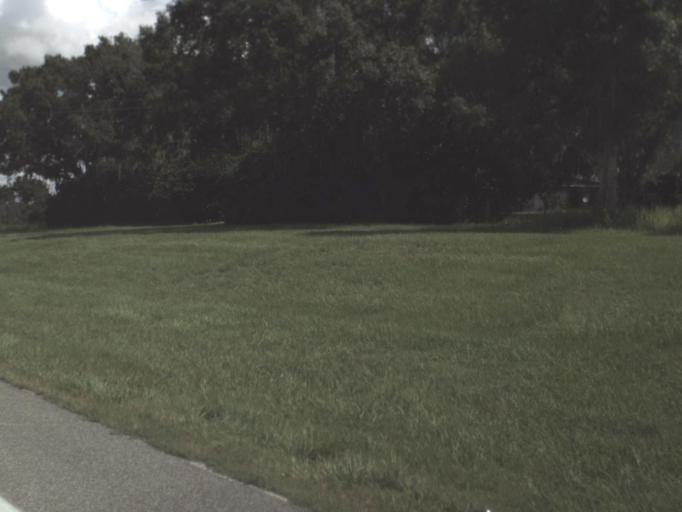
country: US
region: Florida
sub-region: Polk County
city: Polk City
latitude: 28.2778
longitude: -81.8287
